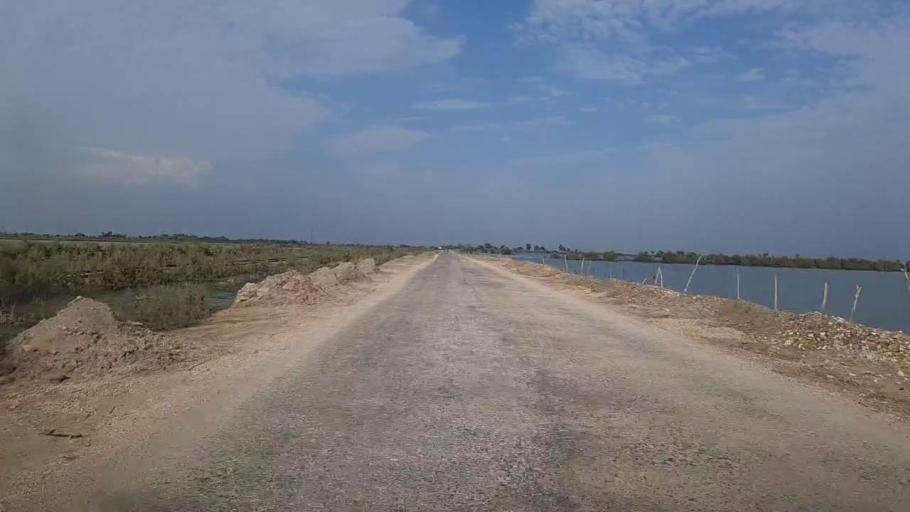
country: PK
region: Sindh
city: Thul
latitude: 28.2756
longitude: 68.8441
